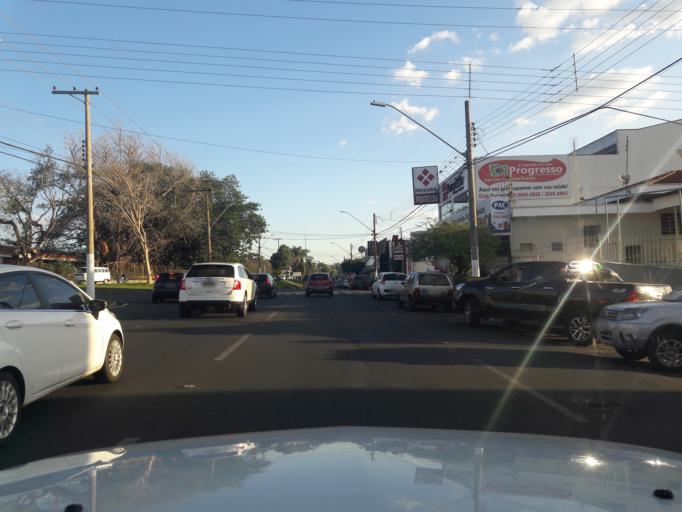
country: BR
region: Sao Paulo
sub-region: Moji-Guacu
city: Mogi-Gaucu
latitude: -22.3913
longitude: -46.9454
